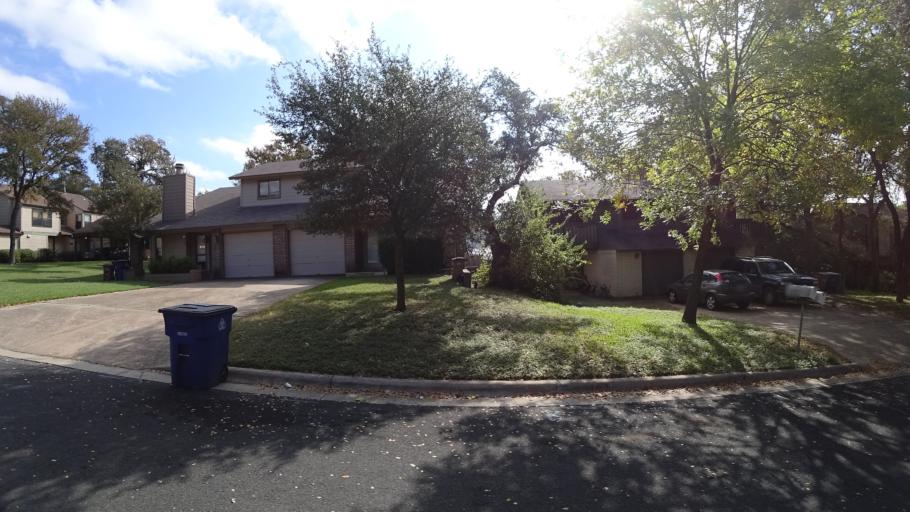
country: US
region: Texas
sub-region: Travis County
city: Manchaca
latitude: 30.1924
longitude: -97.8138
